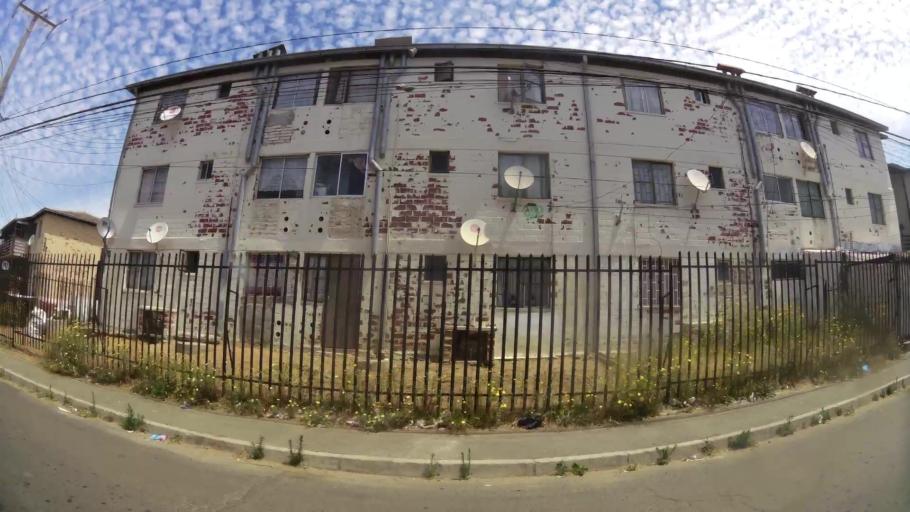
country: CL
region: Valparaiso
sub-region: Provincia de Valparaiso
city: Vina del Mar
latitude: -33.0550
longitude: -71.5708
